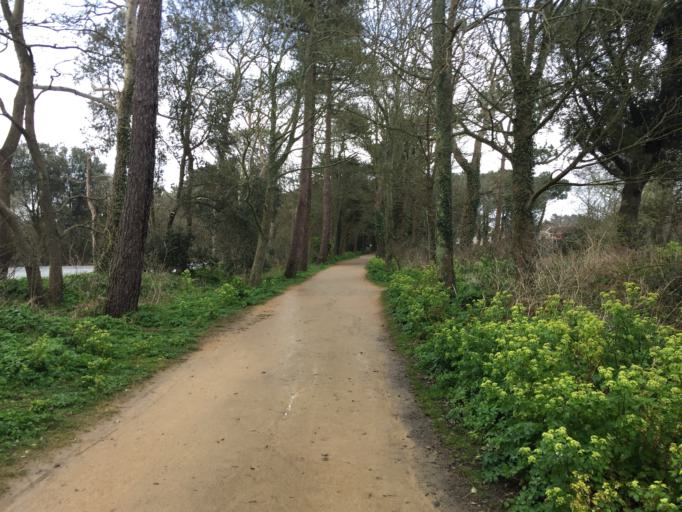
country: JE
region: St Helier
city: Saint Helier
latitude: 49.1874
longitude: -2.2194
